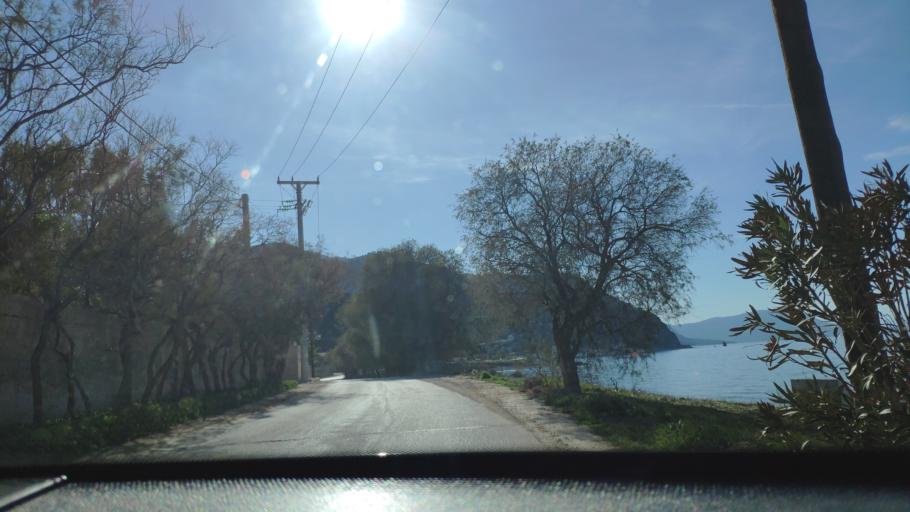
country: GR
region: Attica
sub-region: Nomarchia Dytikis Attikis
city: Kineta
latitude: 38.0683
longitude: 23.1495
